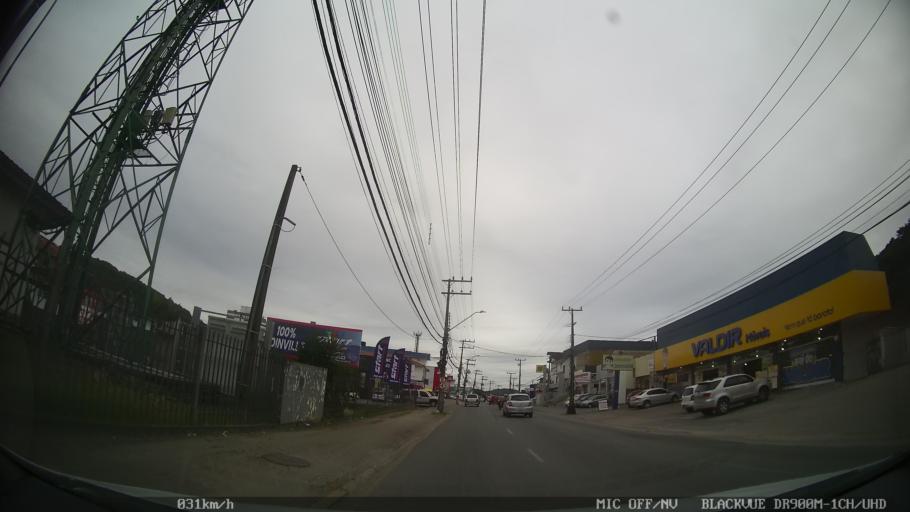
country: BR
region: Santa Catarina
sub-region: Joinville
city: Joinville
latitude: -26.2726
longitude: -48.8289
